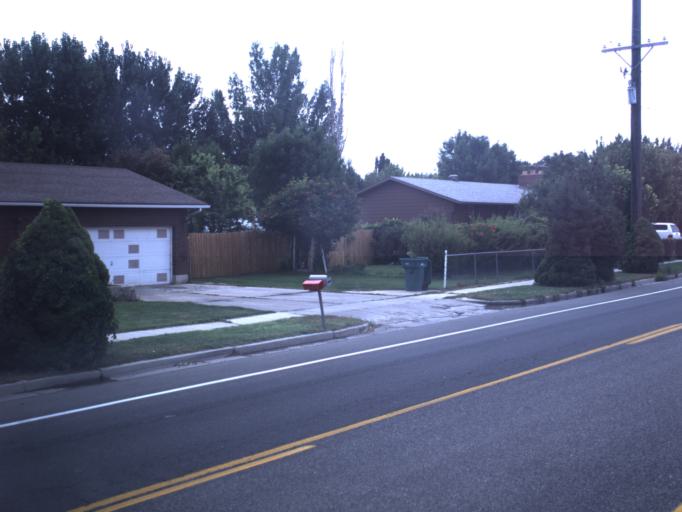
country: US
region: Utah
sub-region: Davis County
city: Clinton
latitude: 41.1663
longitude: -112.0645
